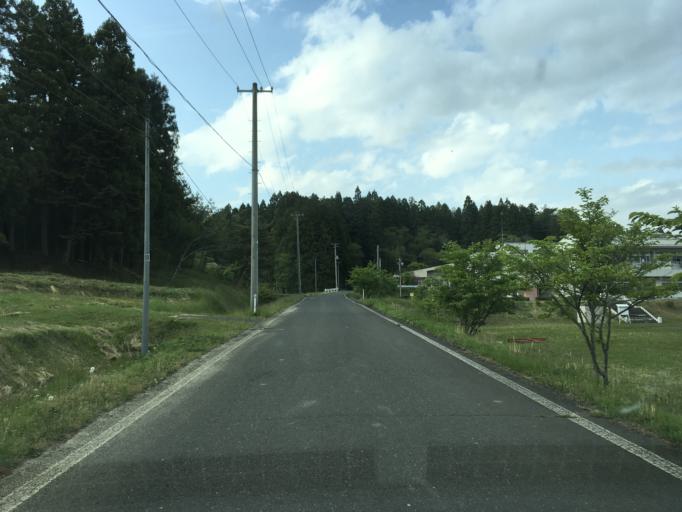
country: JP
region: Iwate
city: Ichinoseki
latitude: 38.8105
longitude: 141.1752
